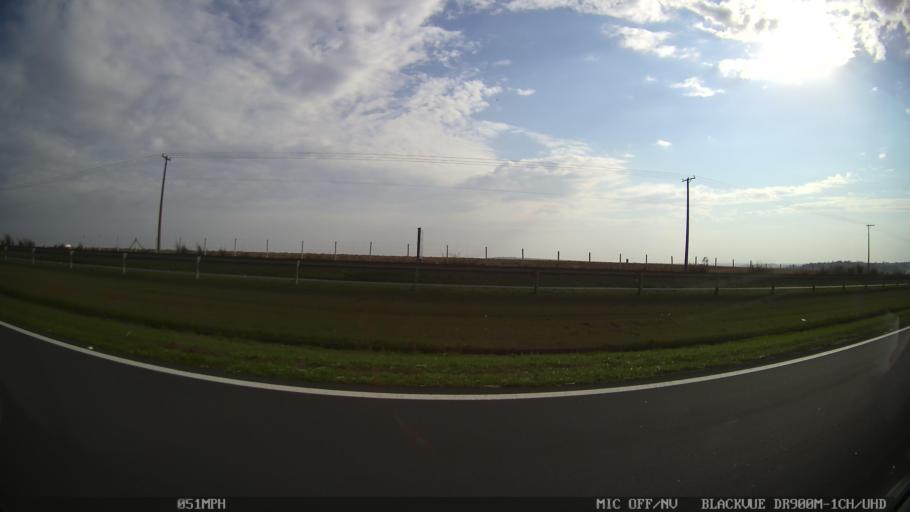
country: BR
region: Sao Paulo
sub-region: Paulinia
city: Paulinia
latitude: -22.7069
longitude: -47.1435
